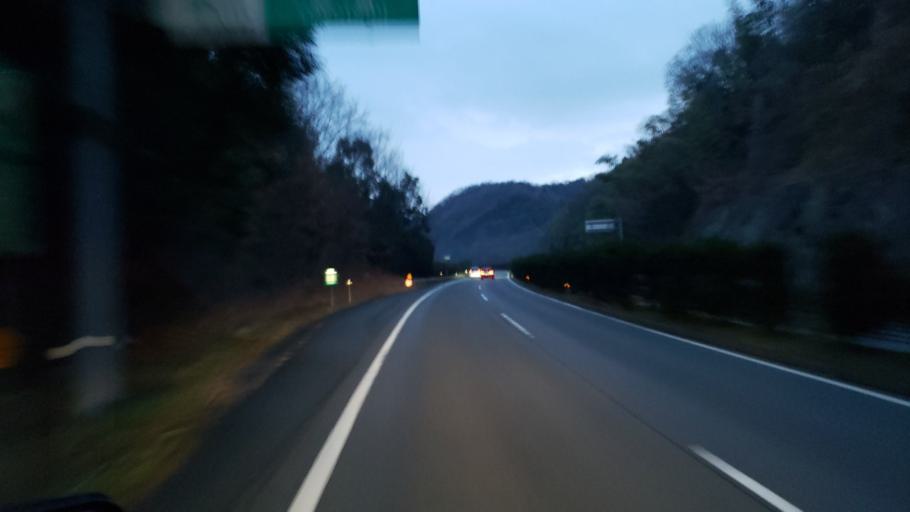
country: JP
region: Hyogo
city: Himeji
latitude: 34.8688
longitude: 134.7401
